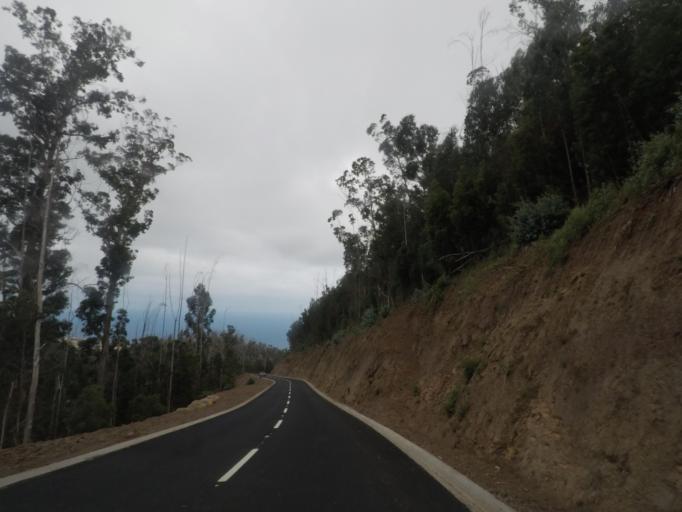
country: PT
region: Madeira
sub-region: Calheta
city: Estreito da Calheta
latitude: 32.7451
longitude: -17.1586
